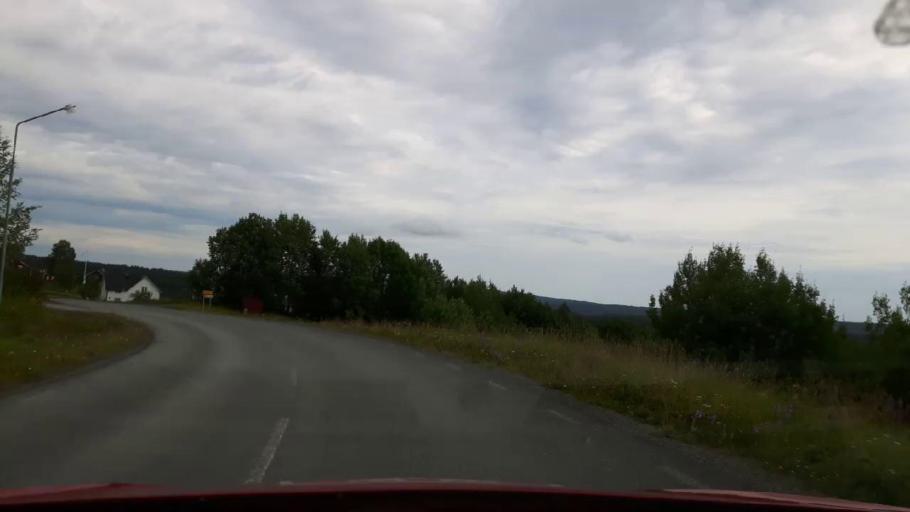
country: SE
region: Jaemtland
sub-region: OEstersunds Kommun
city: Lit
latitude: 63.4222
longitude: 15.2584
